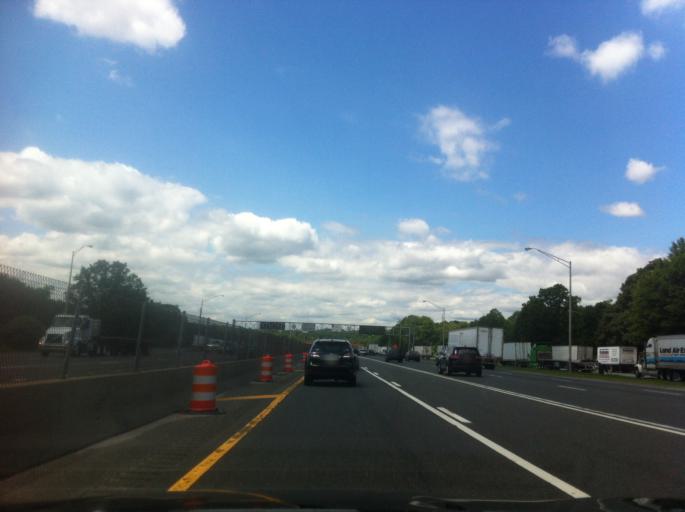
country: US
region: New York
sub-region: Suffolk County
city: Dix Hills
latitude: 40.8037
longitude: -73.3130
